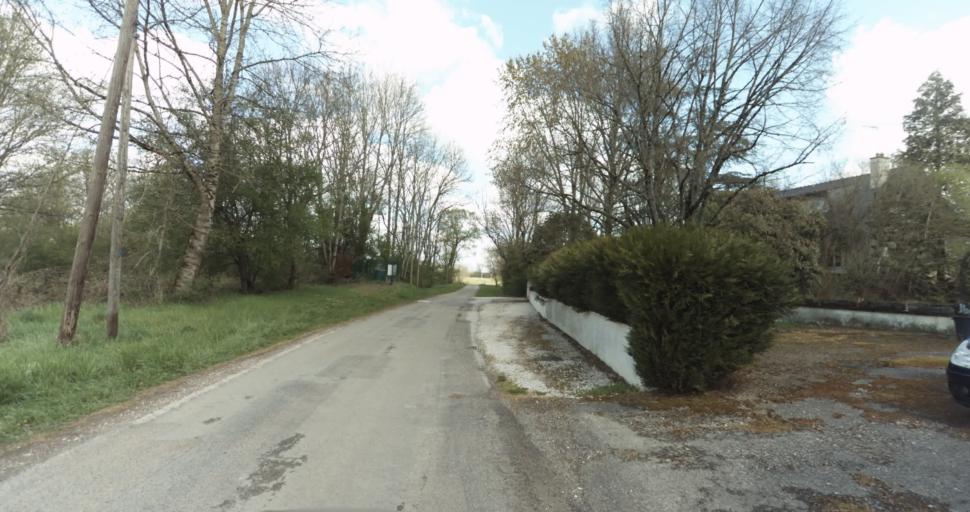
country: FR
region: Bourgogne
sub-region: Departement de la Cote-d'Or
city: Auxonne
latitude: 47.2000
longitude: 5.3919
